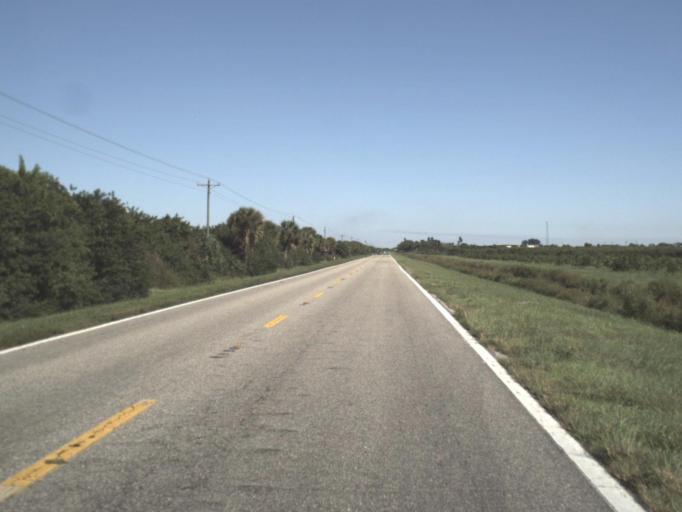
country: US
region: Florida
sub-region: Glades County
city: Moore Haven
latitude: 26.7683
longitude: -81.1942
